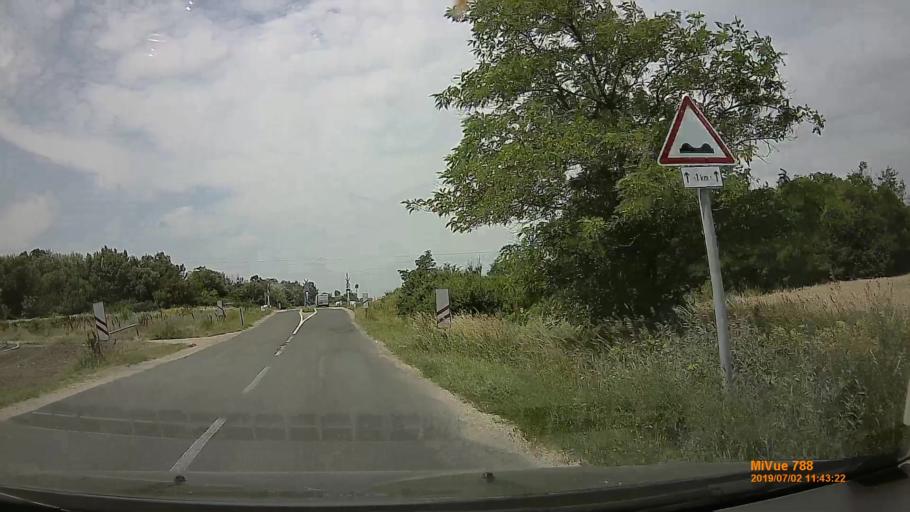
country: HU
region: Gyor-Moson-Sopron
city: Mosonmagyarovar
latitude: 47.8763
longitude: 17.2201
